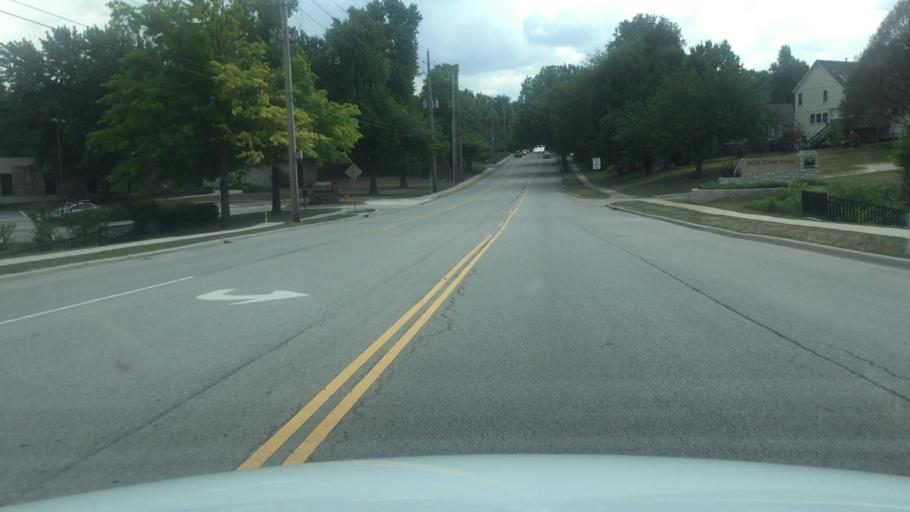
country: US
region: Kansas
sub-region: Johnson County
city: Lenexa
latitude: 38.9694
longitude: -94.7611
